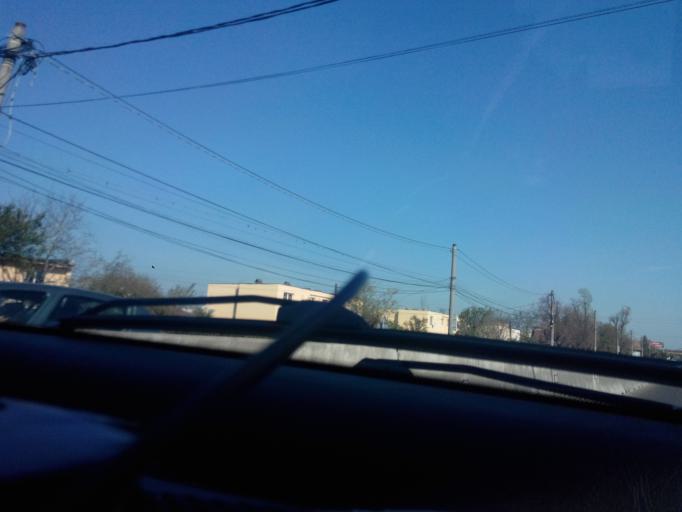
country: RO
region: Ilfov
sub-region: Comuna Corbeanca
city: Corbeanca
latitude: 44.6237
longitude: 26.0694
